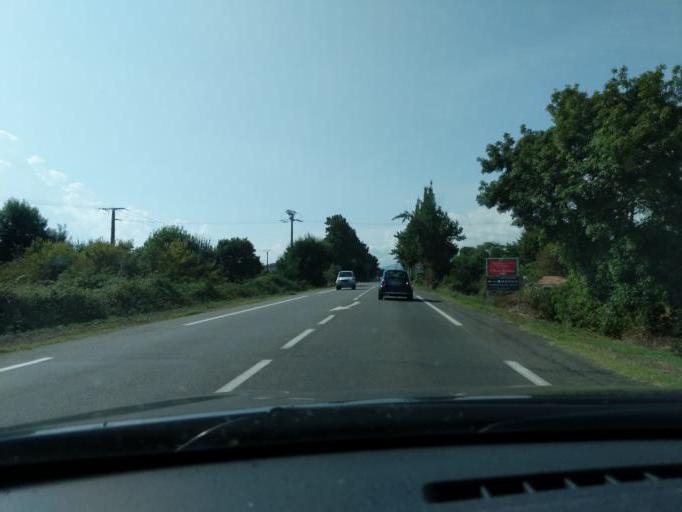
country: FR
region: Corsica
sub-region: Departement de la Haute-Corse
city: Ghisonaccia
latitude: 41.9614
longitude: 9.3969
